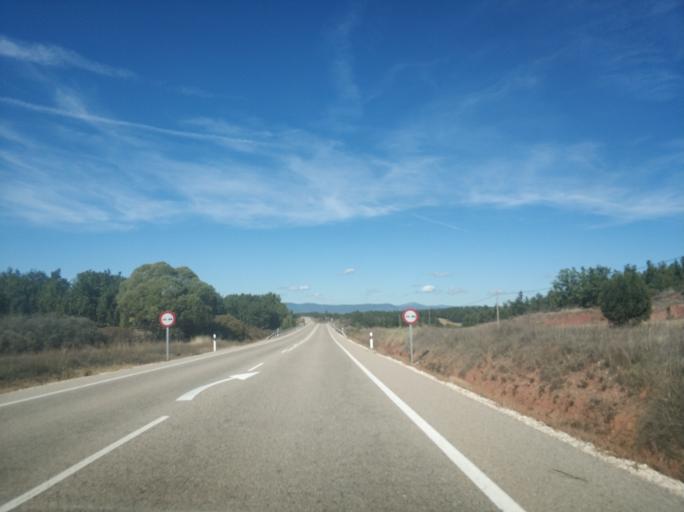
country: ES
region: Castille and Leon
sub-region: Provincia de Burgos
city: Hacinas
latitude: 41.9517
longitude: -3.2916
